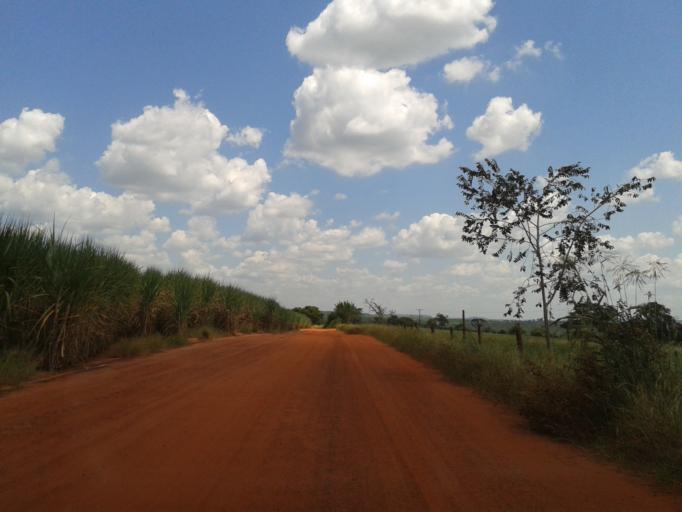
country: BR
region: Minas Gerais
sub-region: Ituiutaba
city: Ituiutaba
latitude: -19.0229
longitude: -49.6902
